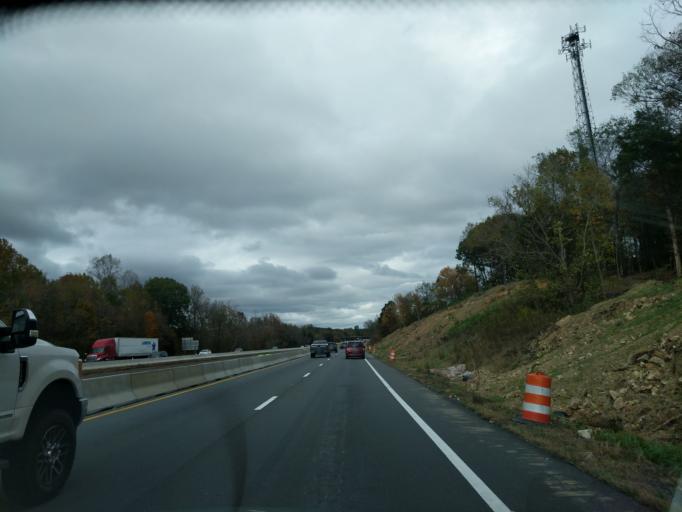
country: US
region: North Carolina
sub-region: Rowan County
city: Landis
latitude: 35.5196
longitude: -80.5703
